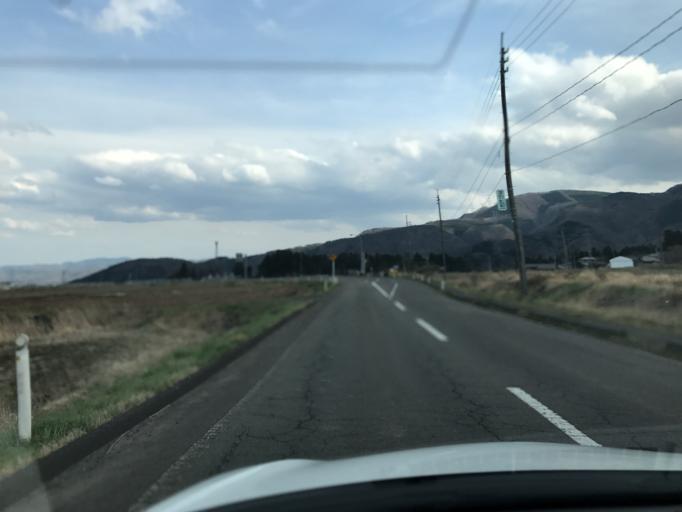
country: JP
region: Miyagi
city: Shiroishi
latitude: 38.0130
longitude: 140.5842
